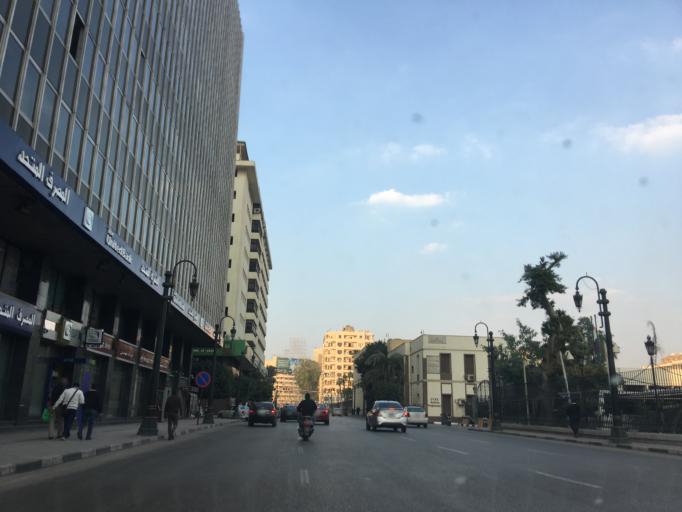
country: EG
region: Muhafazat al Qahirah
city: Cairo
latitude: 30.0410
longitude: 31.2355
